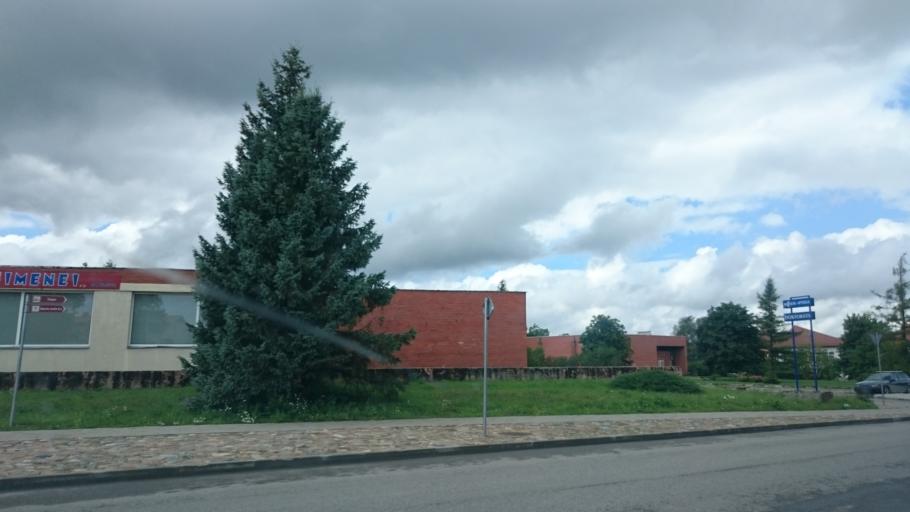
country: LV
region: Aizpute
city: Aizpute
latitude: 56.7195
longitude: 21.6079
